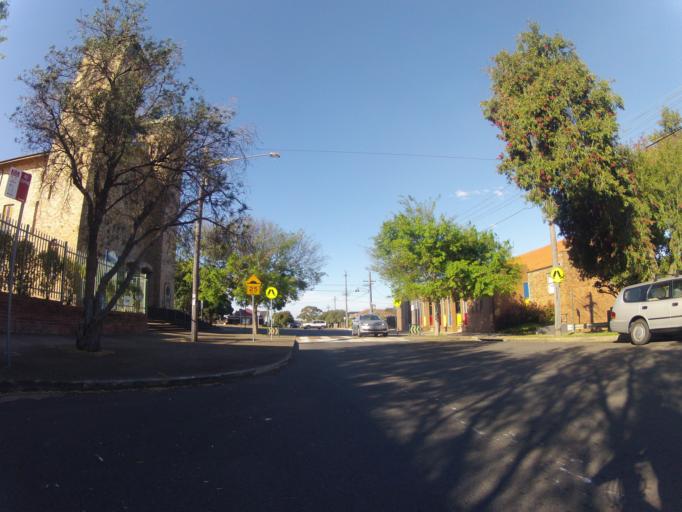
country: AU
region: New South Wales
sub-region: Canterbury
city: Roselands
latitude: -33.9469
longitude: 151.0802
